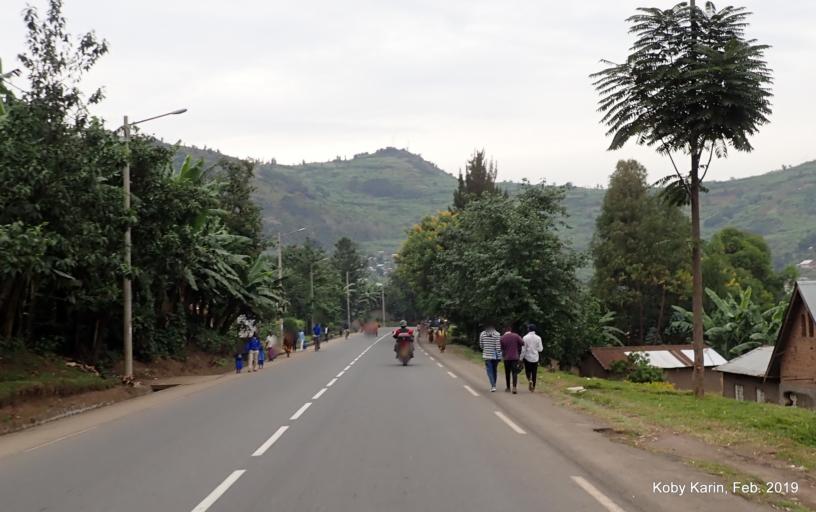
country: RW
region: Western Province
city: Gisenyi
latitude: -1.6938
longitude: 29.3060
